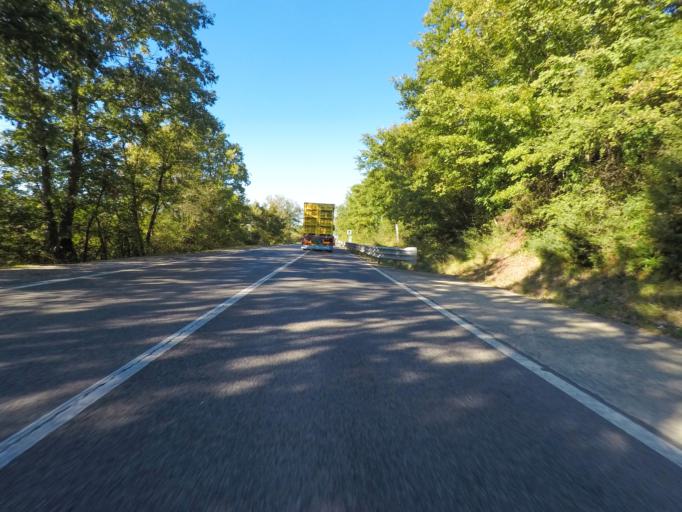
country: IT
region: Tuscany
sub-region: Provincia di Siena
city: Rosia
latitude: 43.1960
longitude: 11.2766
